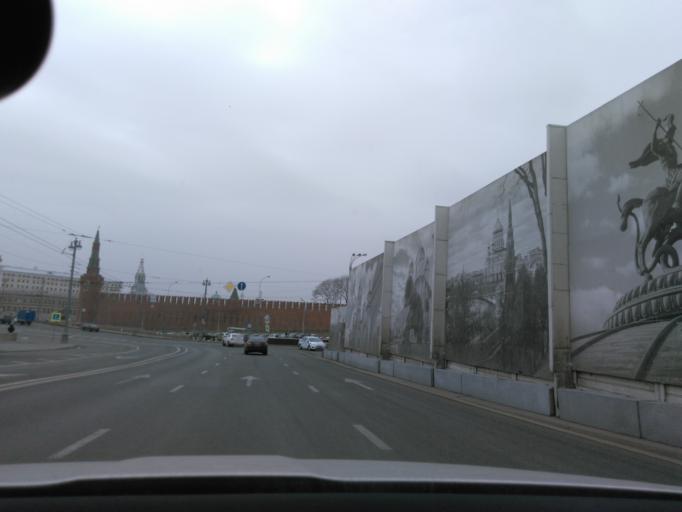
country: RU
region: Moscow
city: Moscow
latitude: 55.7521
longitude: 37.6249
